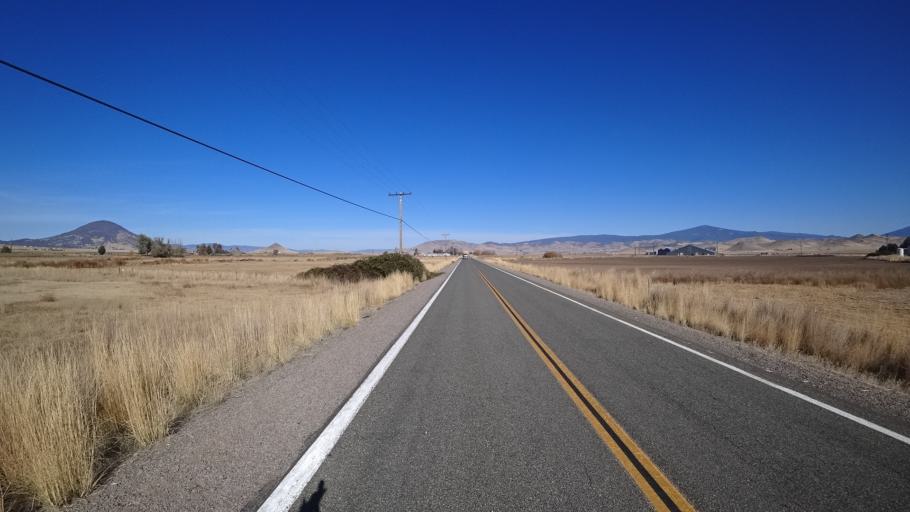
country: US
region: California
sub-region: Siskiyou County
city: Montague
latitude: 41.7665
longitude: -122.4852
